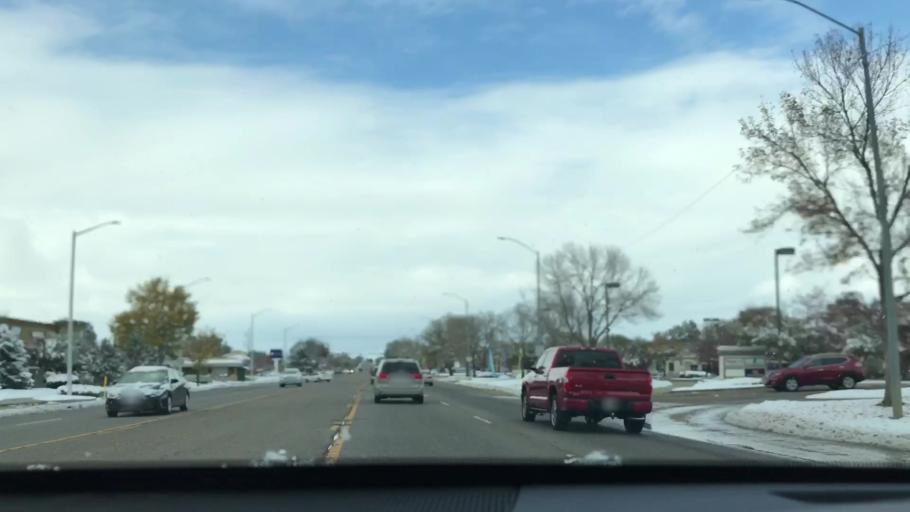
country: US
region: Colorado
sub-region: Boulder County
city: Longmont
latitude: 40.1897
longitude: -105.1023
